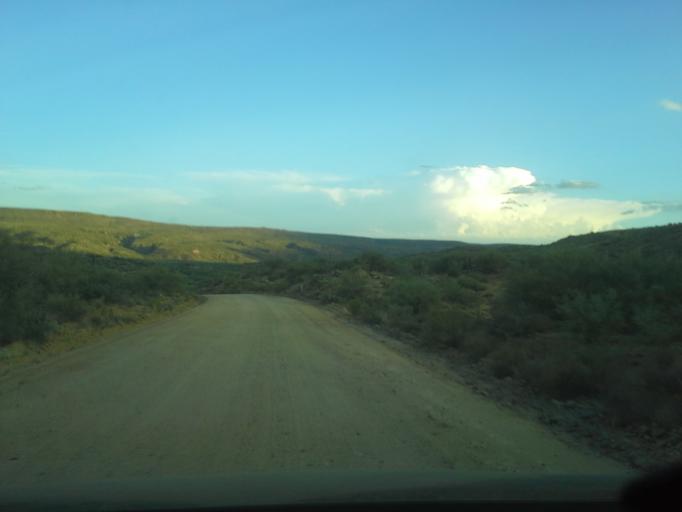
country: US
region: Arizona
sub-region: Yavapai County
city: Cordes Lakes
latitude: 34.2287
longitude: -112.1545
